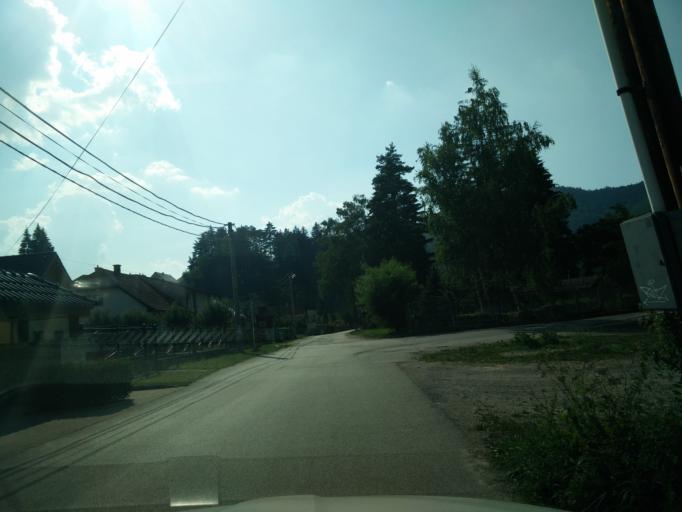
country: SK
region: Zilinsky
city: Rajec
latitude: 49.1304
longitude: 18.6921
